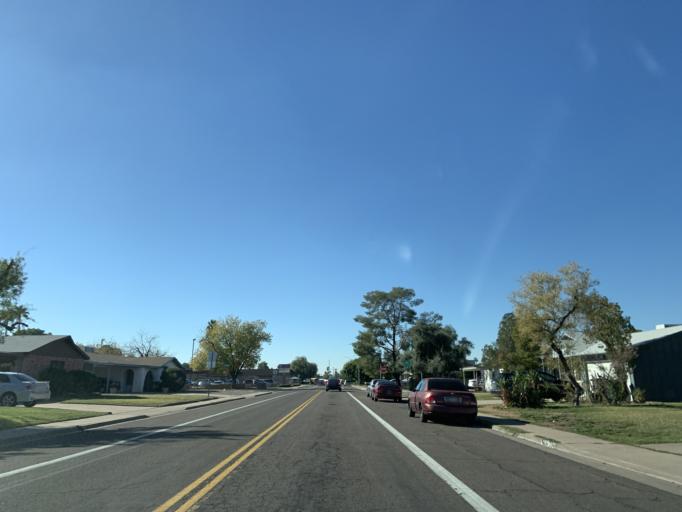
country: US
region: Arizona
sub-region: Maricopa County
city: Tempe
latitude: 33.4003
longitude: -111.8801
